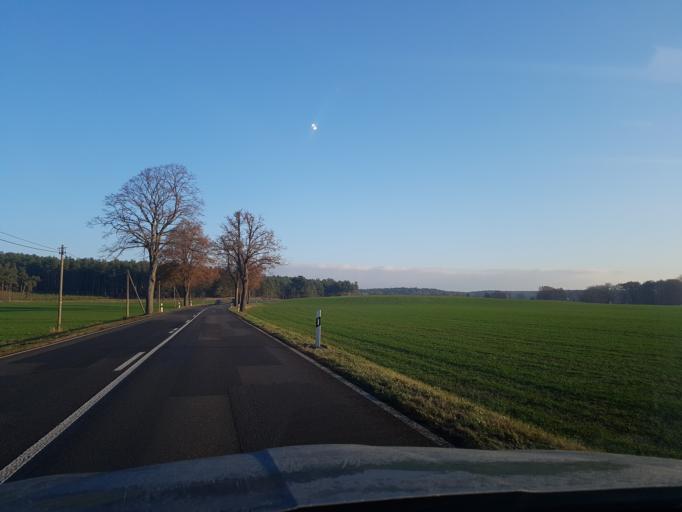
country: DE
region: Brandenburg
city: Schlieben
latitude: 51.7356
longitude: 13.4275
